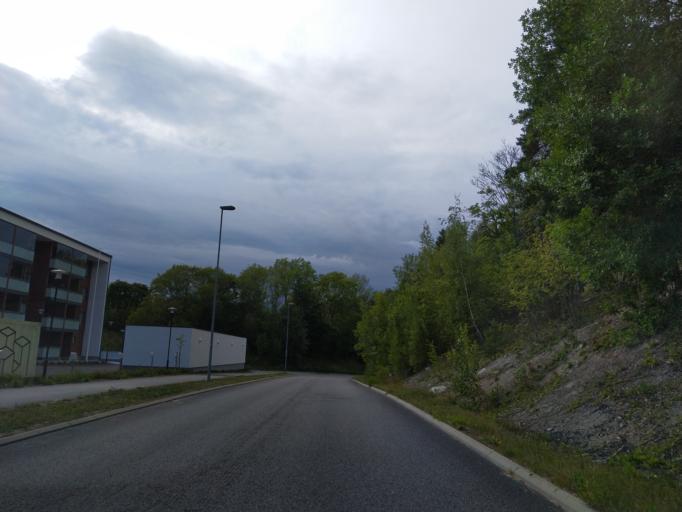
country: FI
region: Varsinais-Suomi
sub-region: Turku
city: Turku
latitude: 60.4259
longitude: 22.2065
